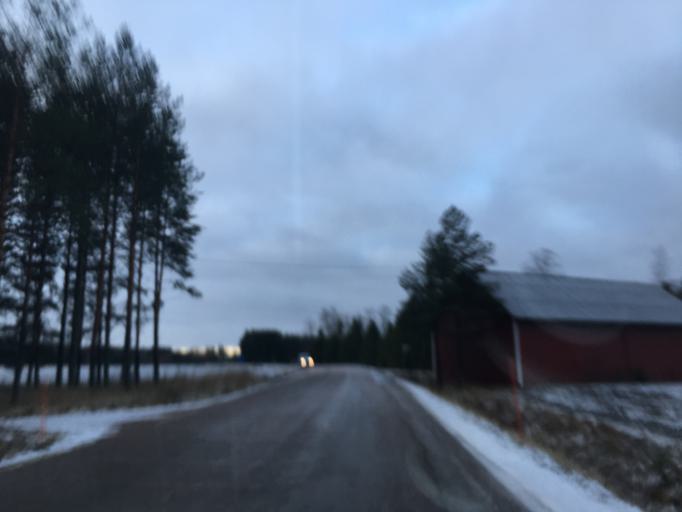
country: FI
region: Varsinais-Suomi
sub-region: Loimaa
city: Aura
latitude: 60.6126
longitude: 22.5723
